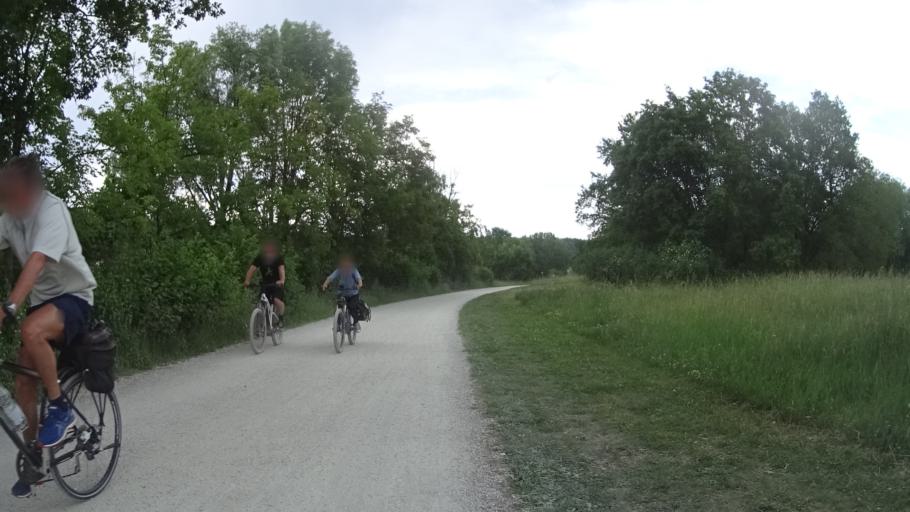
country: DE
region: Bavaria
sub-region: Upper Palatinate
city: Sinzing
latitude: 49.0281
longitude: 12.0534
